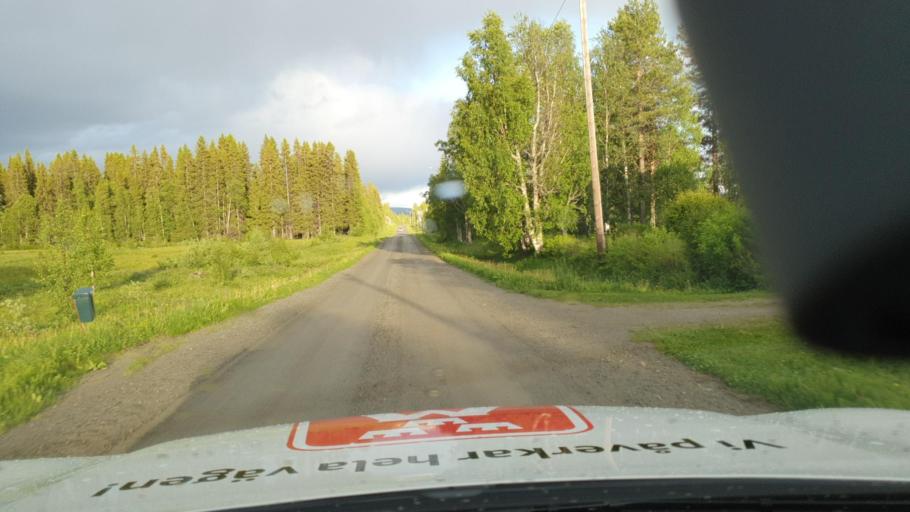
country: SE
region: Vaesterbotten
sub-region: Storumans Kommun
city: Storuman
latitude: 64.7636
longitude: 17.0611
